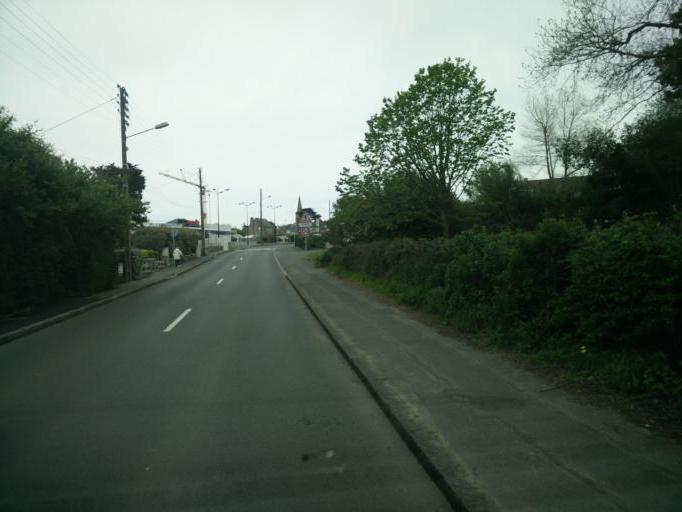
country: FR
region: Brittany
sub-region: Departement des Cotes-d'Armor
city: Trebeurden
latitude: 48.7700
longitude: -3.5717
